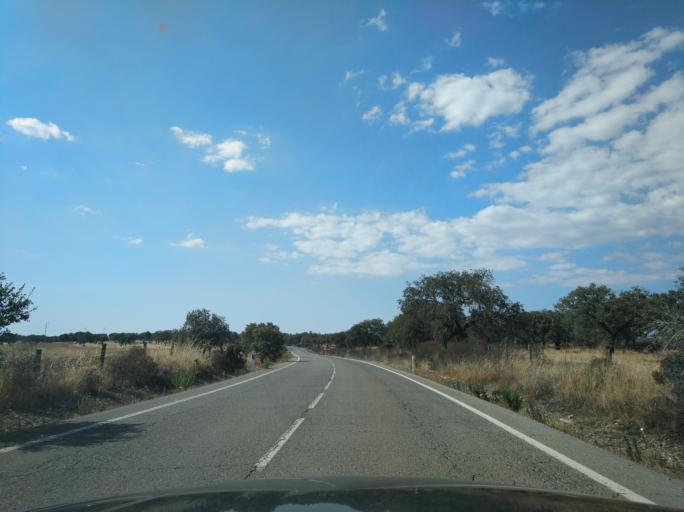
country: ES
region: Andalusia
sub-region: Provincia de Huelva
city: Santa Barbara de Casa
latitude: 37.7648
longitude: -7.1374
